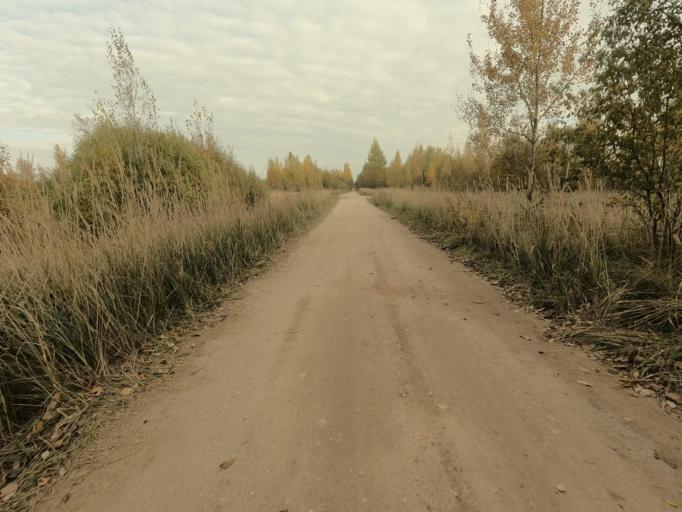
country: RU
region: Novgorod
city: Pankovka
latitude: 58.8980
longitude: 30.9951
